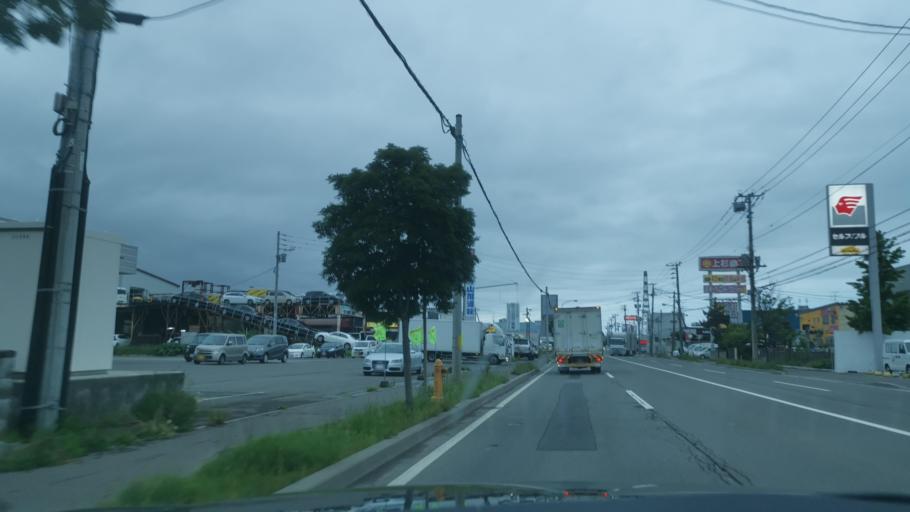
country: JP
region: Hokkaido
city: Sapporo
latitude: 43.1072
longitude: 141.2814
